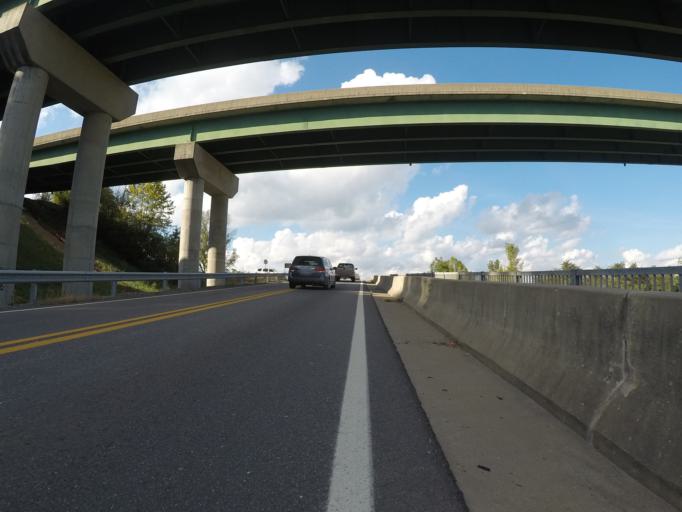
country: US
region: Ohio
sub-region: Lawrence County
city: Burlington
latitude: 38.3953
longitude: -82.5162
